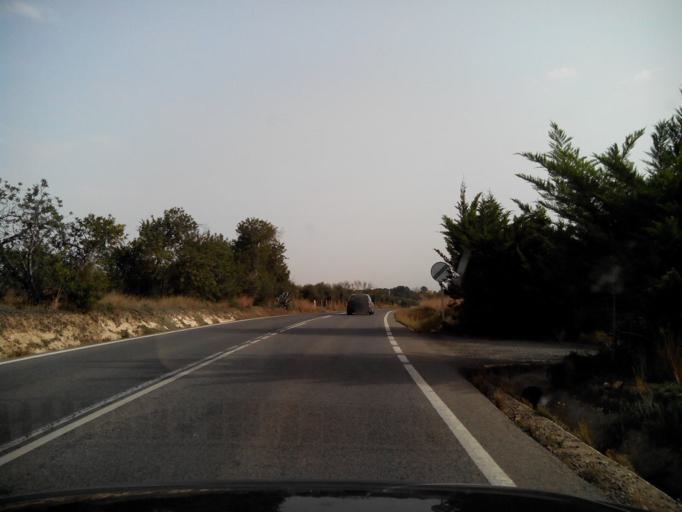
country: ES
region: Catalonia
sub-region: Provincia de Tarragona
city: Riudoms
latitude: 41.1089
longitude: 1.0880
